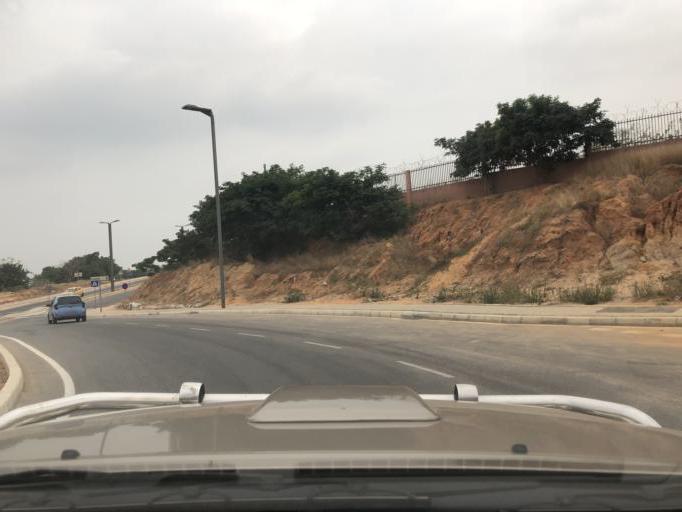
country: AO
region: Luanda
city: Luanda
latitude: -8.8985
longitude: 13.1755
